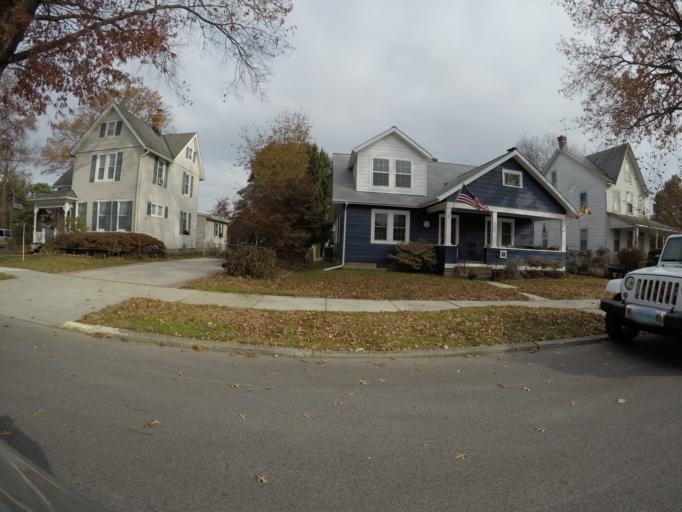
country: US
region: Maryland
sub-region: Harford County
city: Havre de Grace
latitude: 39.5412
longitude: -76.0896
